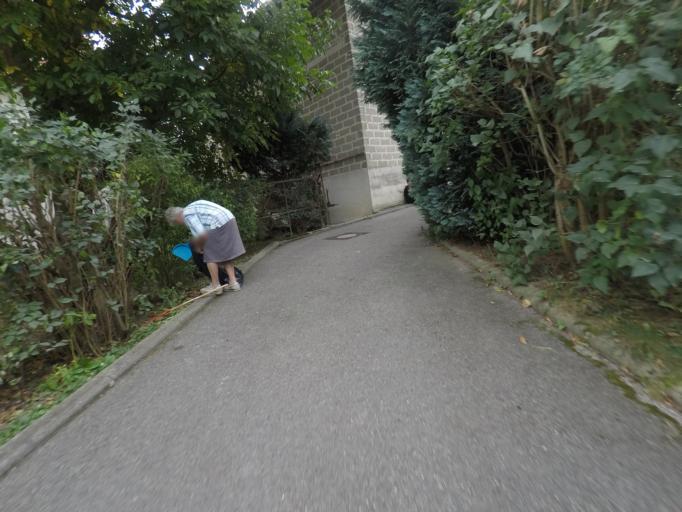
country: DE
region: Baden-Wuerttemberg
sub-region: Regierungsbezirk Stuttgart
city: Herrenberg
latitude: 48.5838
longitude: 8.8371
